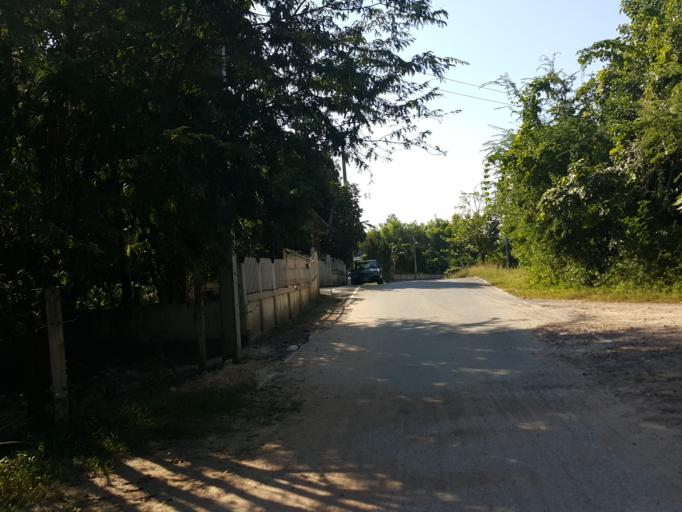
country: TH
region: Chiang Mai
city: Mae On
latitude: 18.7907
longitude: 99.1893
